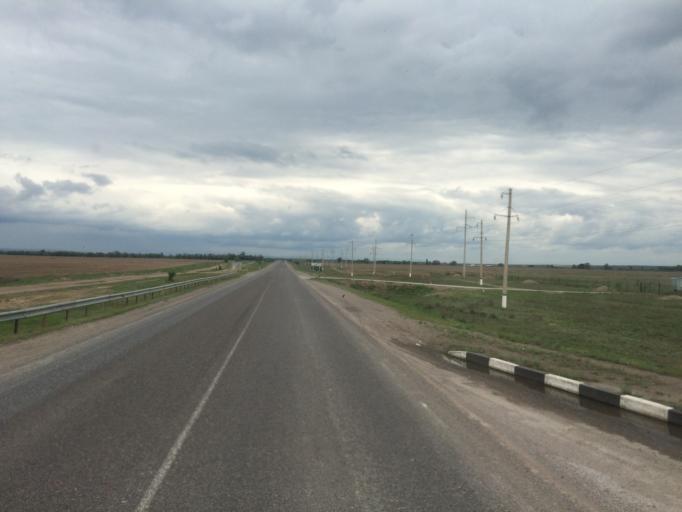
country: KG
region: Chuy
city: Sokuluk
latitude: 43.2461
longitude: 74.3019
